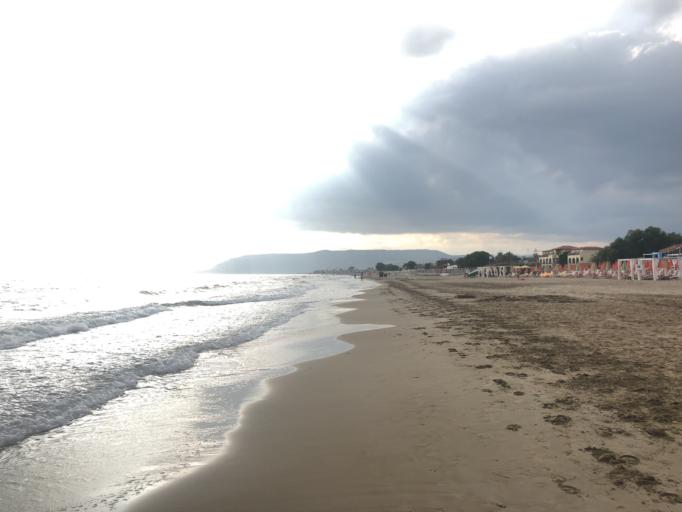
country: GR
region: Crete
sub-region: Nomos Chanias
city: Georgioupolis
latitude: 35.3543
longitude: 24.2937
